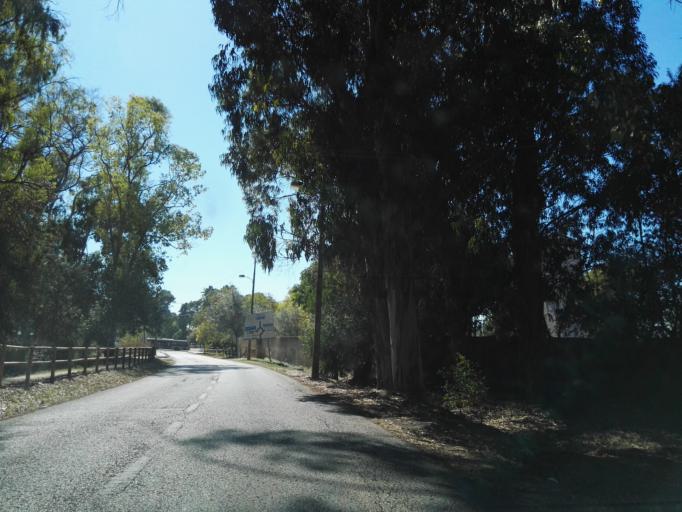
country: PT
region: Lisbon
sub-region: Odivelas
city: Pontinha
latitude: 38.7377
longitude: -9.2005
